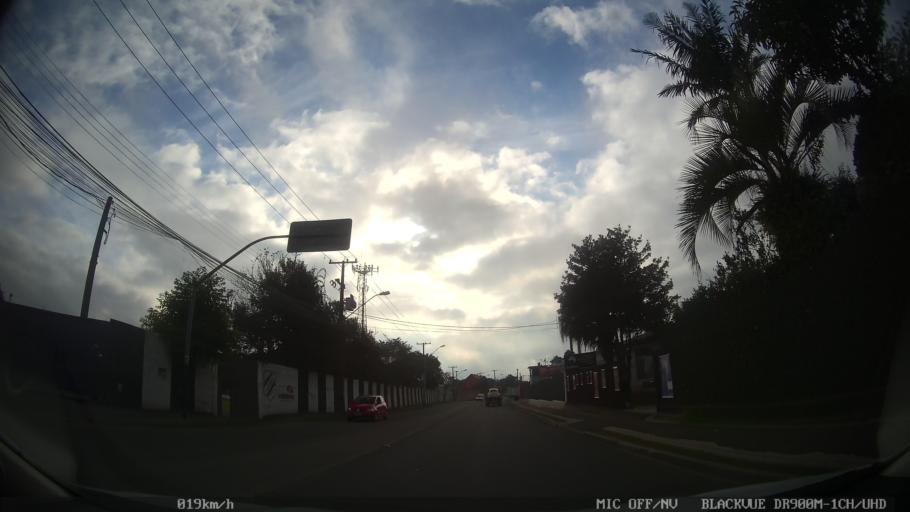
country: BR
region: Parana
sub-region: Almirante Tamandare
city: Almirante Tamandare
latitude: -25.3951
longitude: -49.3465
